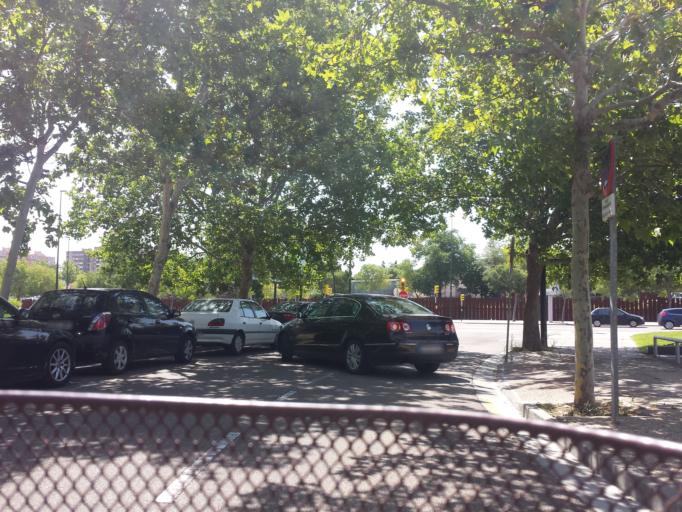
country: ES
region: Aragon
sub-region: Provincia de Zaragoza
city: Delicias
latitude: 41.6401
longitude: -0.9175
